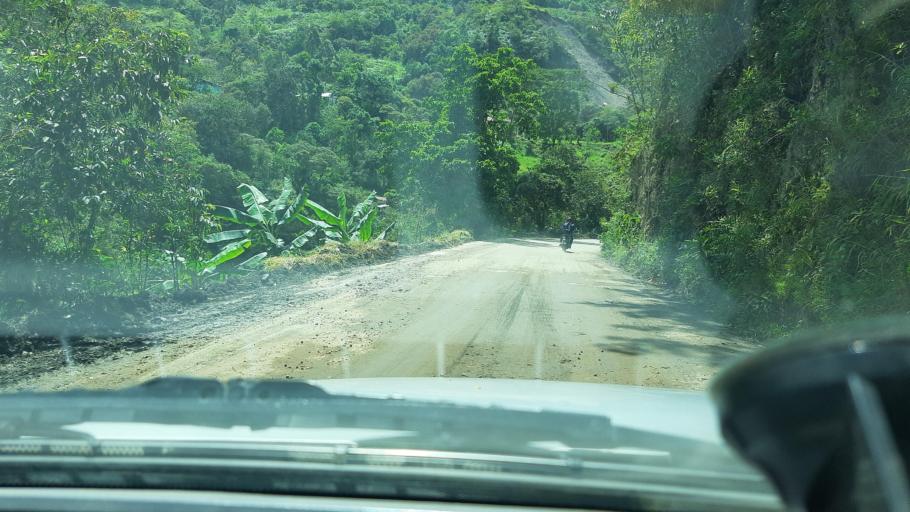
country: CO
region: Boyaca
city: Chinavita
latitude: 5.1848
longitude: -73.3824
